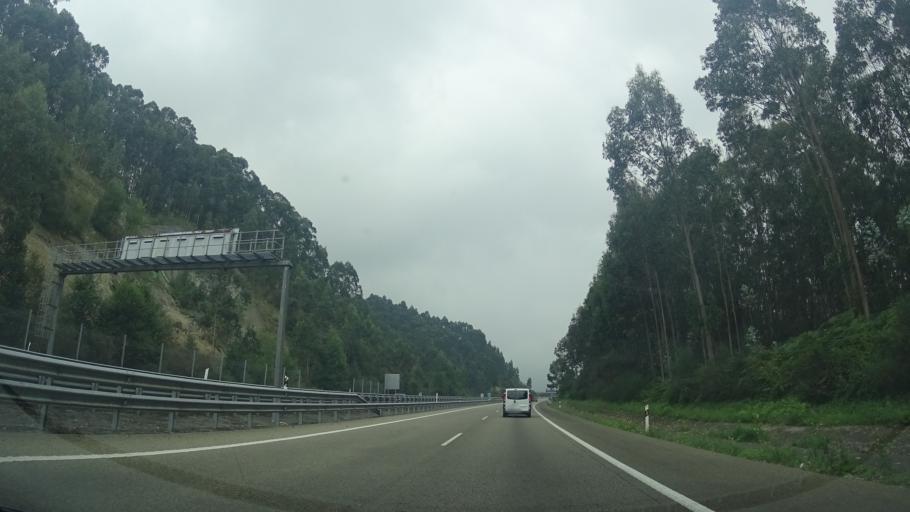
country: ES
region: Asturias
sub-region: Province of Asturias
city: Arriba
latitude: 43.5016
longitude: -5.5407
